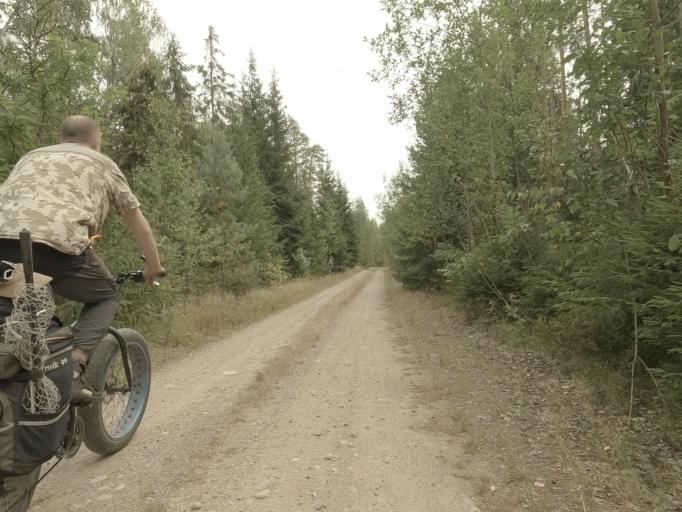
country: RU
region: Leningrad
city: Kamennogorsk
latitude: 61.0174
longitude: 29.2024
